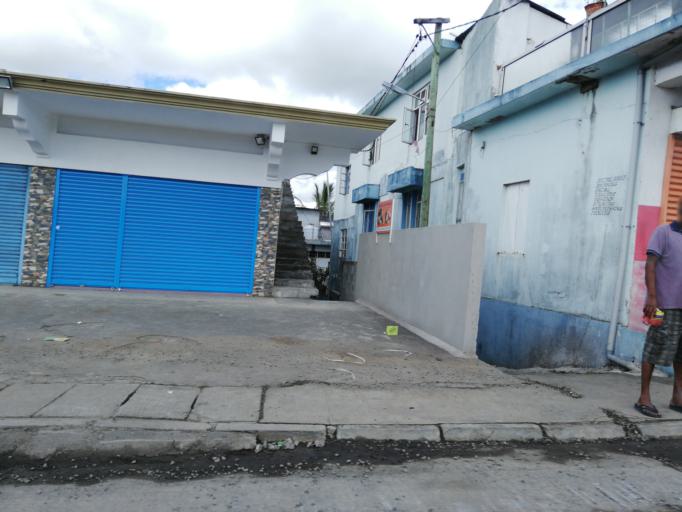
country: MU
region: Flacq
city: Bon Accueil
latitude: -20.1748
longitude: 57.6712
